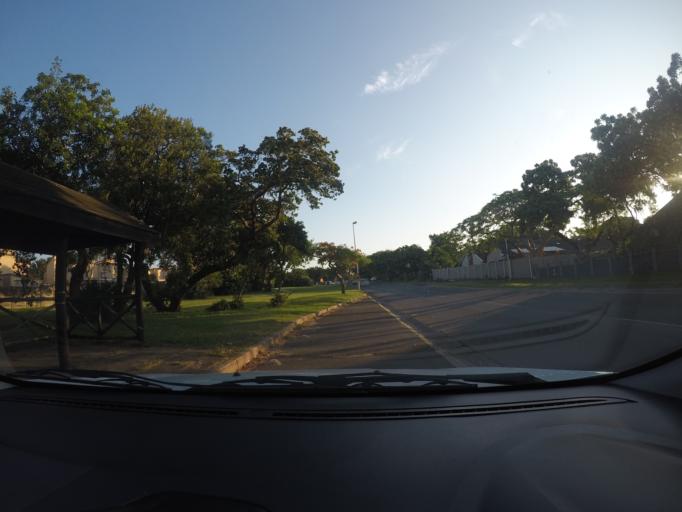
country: ZA
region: KwaZulu-Natal
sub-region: uThungulu District Municipality
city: Richards Bay
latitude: -28.7800
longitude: 32.0997
